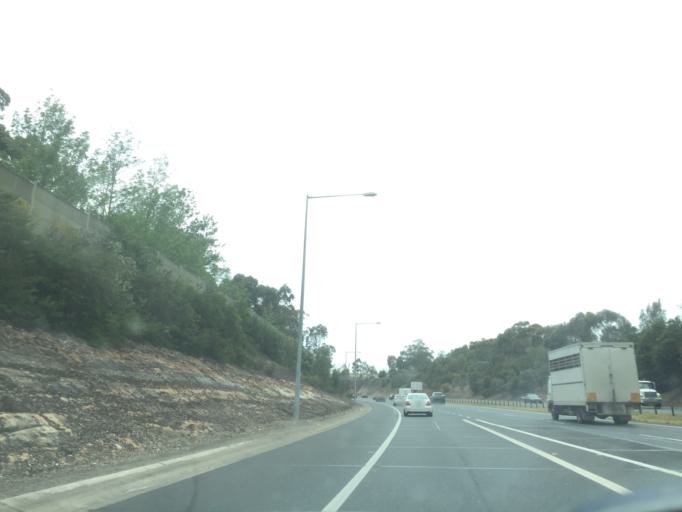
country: AU
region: New South Wales
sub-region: Parramatta
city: Northmead
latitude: -33.7683
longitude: 150.9657
